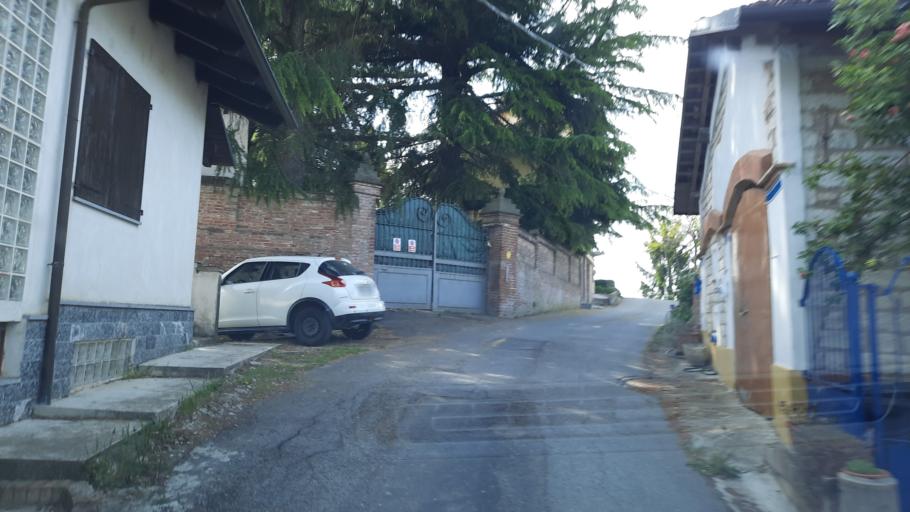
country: IT
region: Piedmont
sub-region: Provincia di Vercelli
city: Palazzolo Vercellese
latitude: 45.1679
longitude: 8.2542
